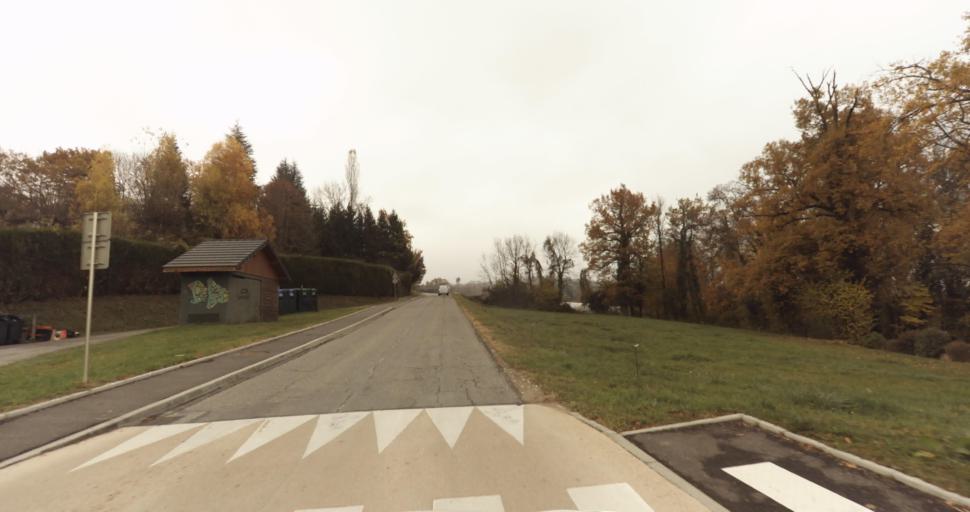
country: FR
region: Rhone-Alpes
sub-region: Departement de la Haute-Savoie
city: Saint-Felix
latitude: 45.7839
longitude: 5.9889
